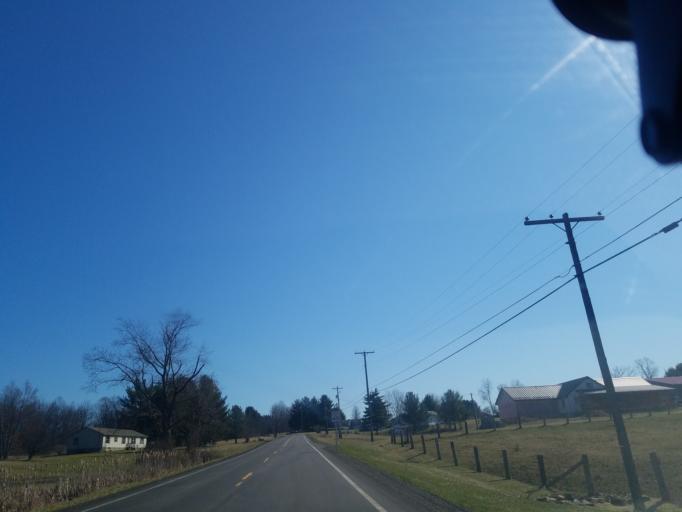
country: US
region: Ohio
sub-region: Tuscarawas County
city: Rockford
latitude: 40.5653
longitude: -81.3516
